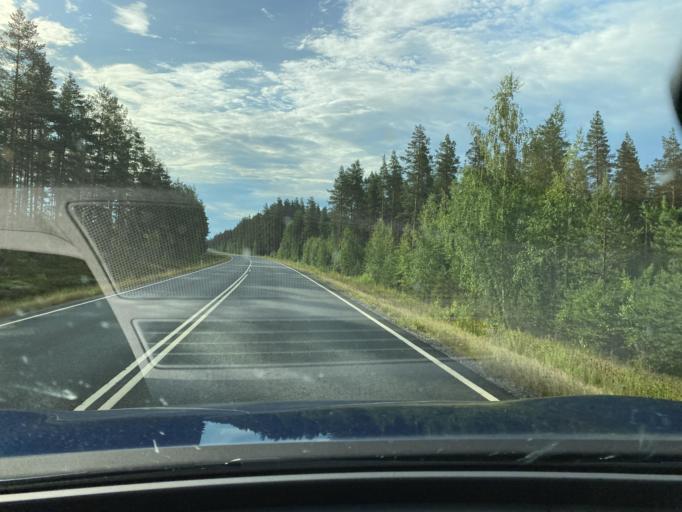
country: FI
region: Central Ostrobothnia
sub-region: Kaustinen
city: Veteli
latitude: 63.4109
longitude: 23.9590
